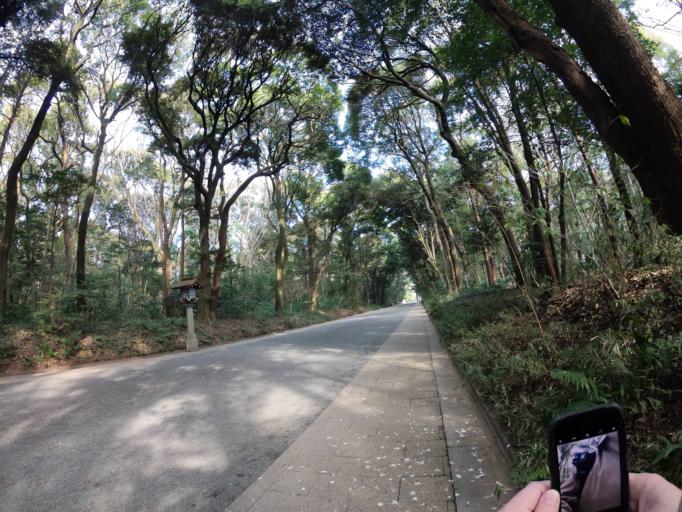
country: JP
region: Chiba
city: Ichihara
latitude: 35.4601
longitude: 140.0181
